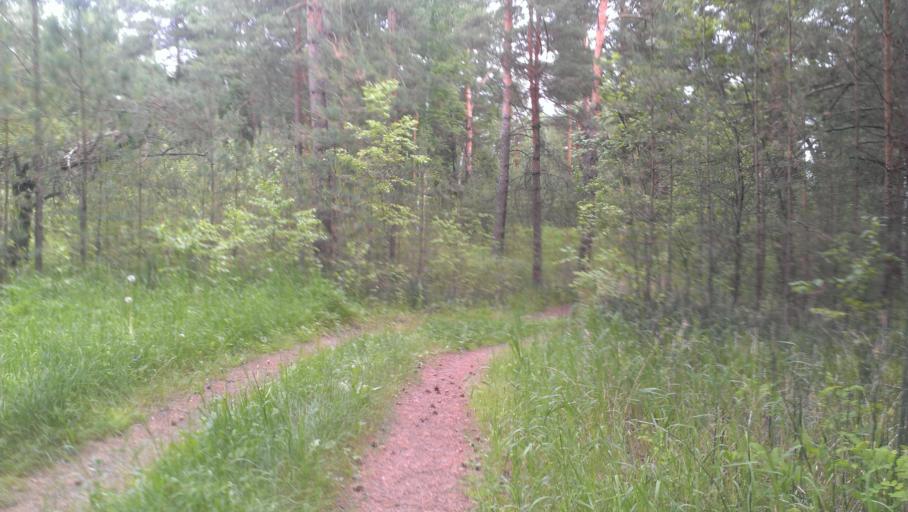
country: RU
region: Altai Krai
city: Sannikovo
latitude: 53.3494
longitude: 84.0369
